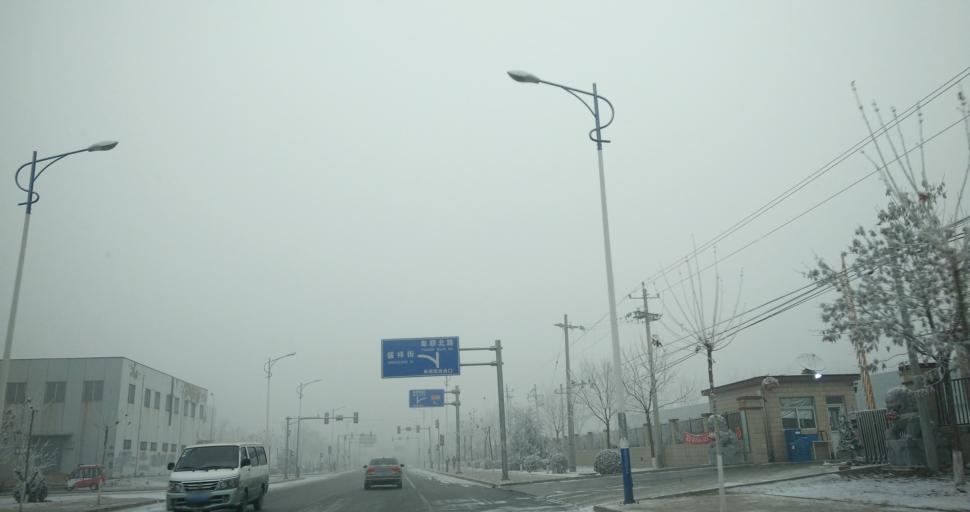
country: CN
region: Beijing
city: Yinghai
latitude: 39.7021
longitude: 116.4148
